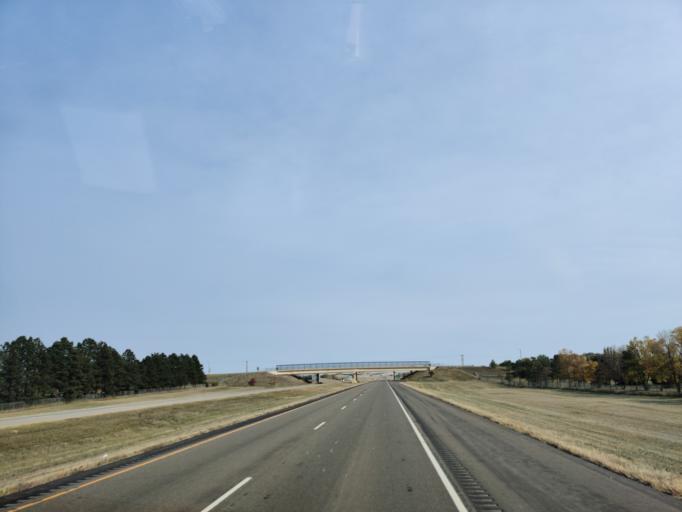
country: US
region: North Dakota
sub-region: Stark County
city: Dickinson
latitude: 46.8949
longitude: -102.7725
